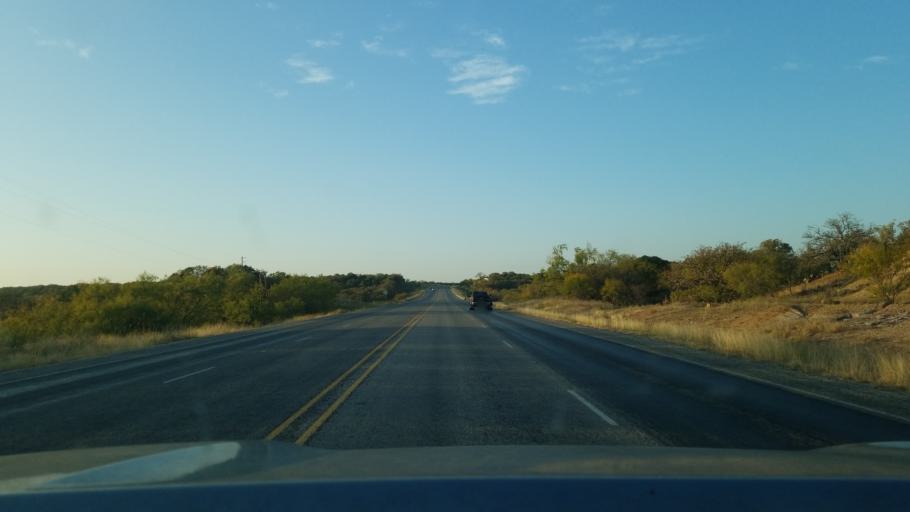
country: US
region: Texas
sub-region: Eastland County
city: Cisco
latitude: 32.3518
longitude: -98.9644
